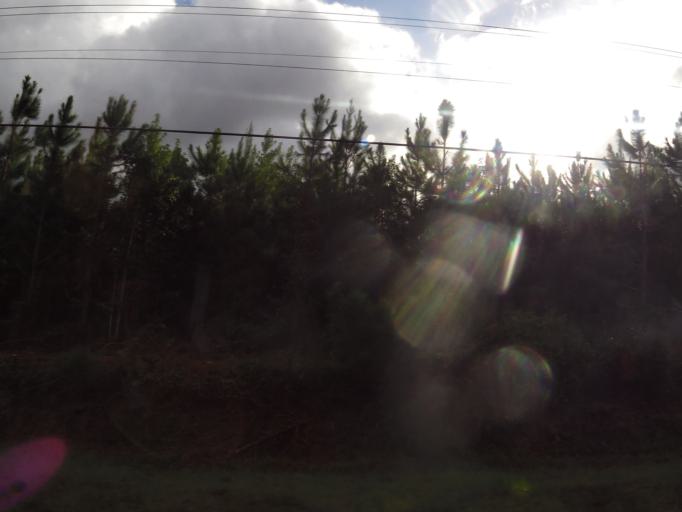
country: US
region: Georgia
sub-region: Liberty County
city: Midway
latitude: 31.8626
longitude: -81.4335
